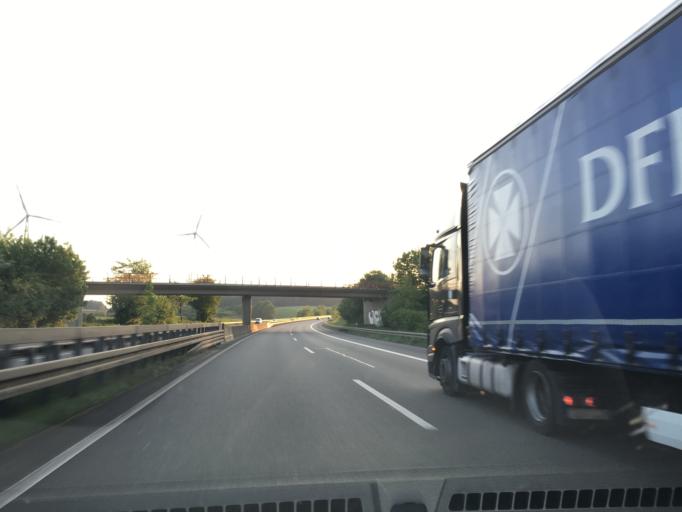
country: DE
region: Lower Saxony
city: Melle
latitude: 52.2154
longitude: 8.2537
